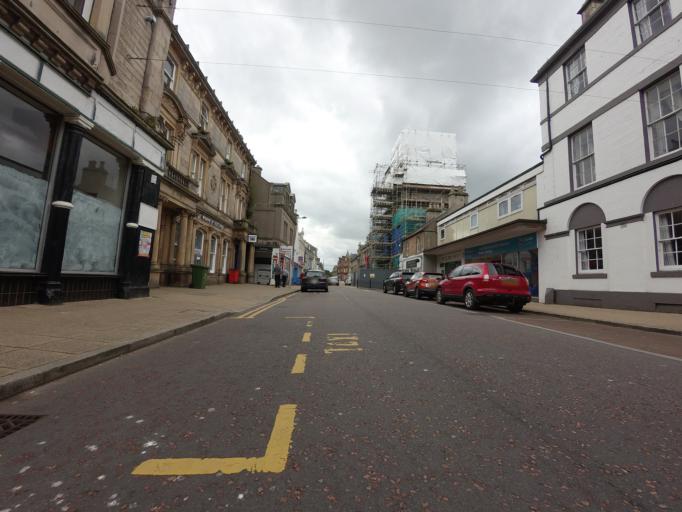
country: GB
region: Scotland
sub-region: Highland
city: Nairn
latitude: 57.5851
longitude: -3.8678
